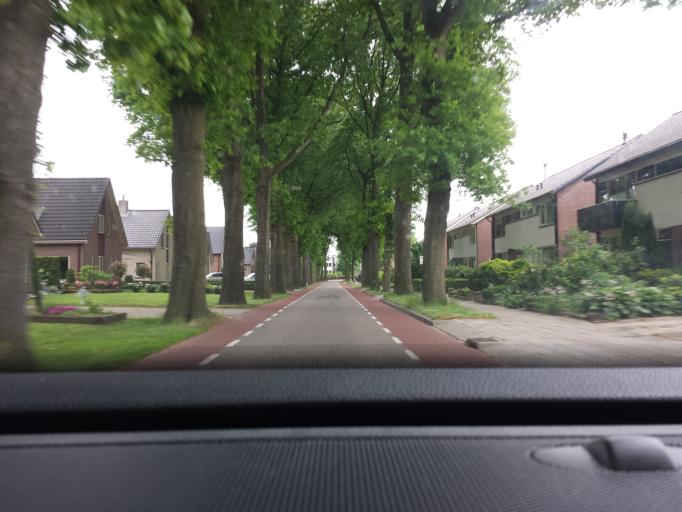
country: NL
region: Gelderland
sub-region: Gemeente Bronckhorst
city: Zelhem
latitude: 52.0105
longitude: 6.3459
